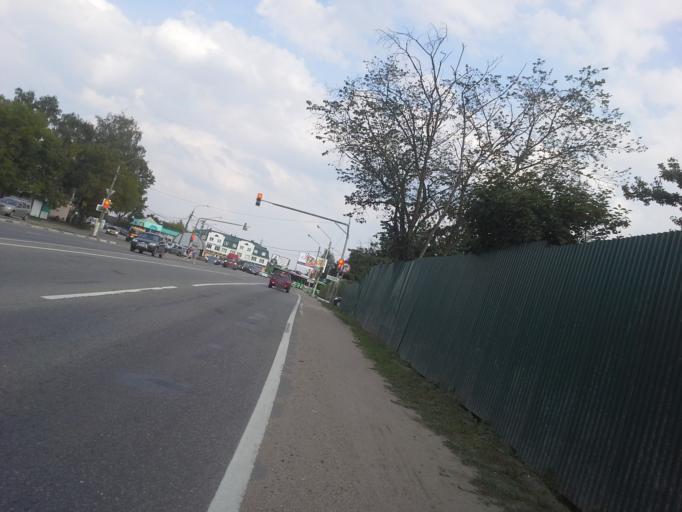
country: RU
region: Moskovskaya
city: Istra
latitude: 55.9129
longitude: 36.8223
